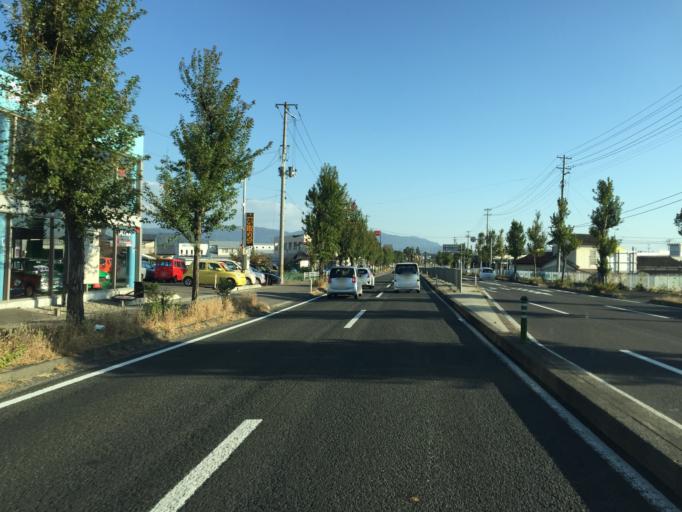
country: JP
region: Fukushima
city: Hobaramachi
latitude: 37.8204
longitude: 140.5050
